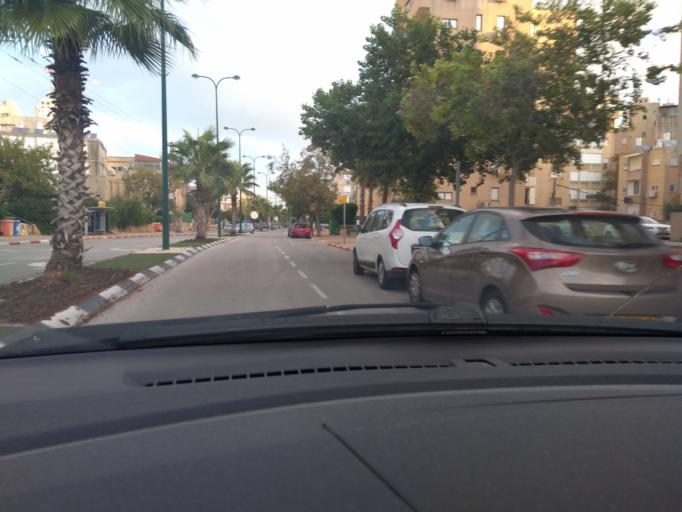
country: IL
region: Central District
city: Netanya
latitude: 32.3356
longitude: 34.8562
